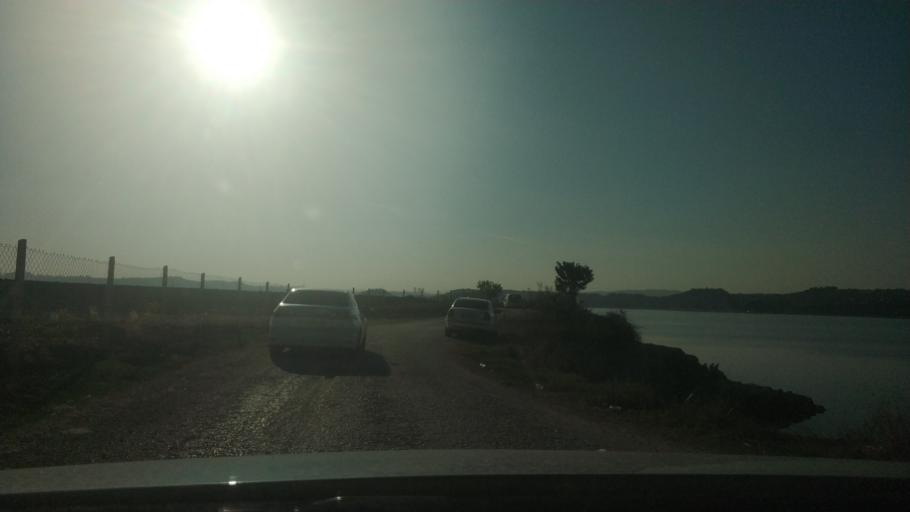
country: TR
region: Adana
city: Adana
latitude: 37.0961
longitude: 35.3017
